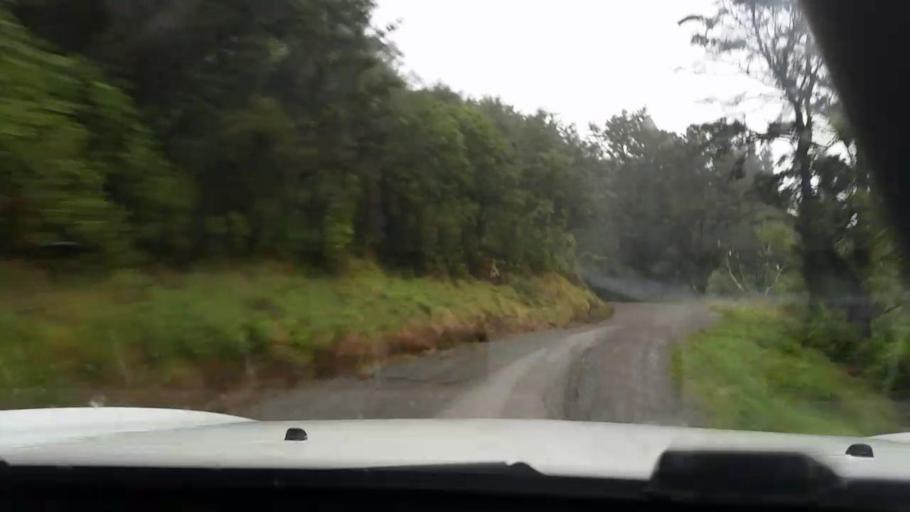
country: NZ
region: Wellington
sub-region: Masterton District
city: Masterton
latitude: -41.1860
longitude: 175.8203
